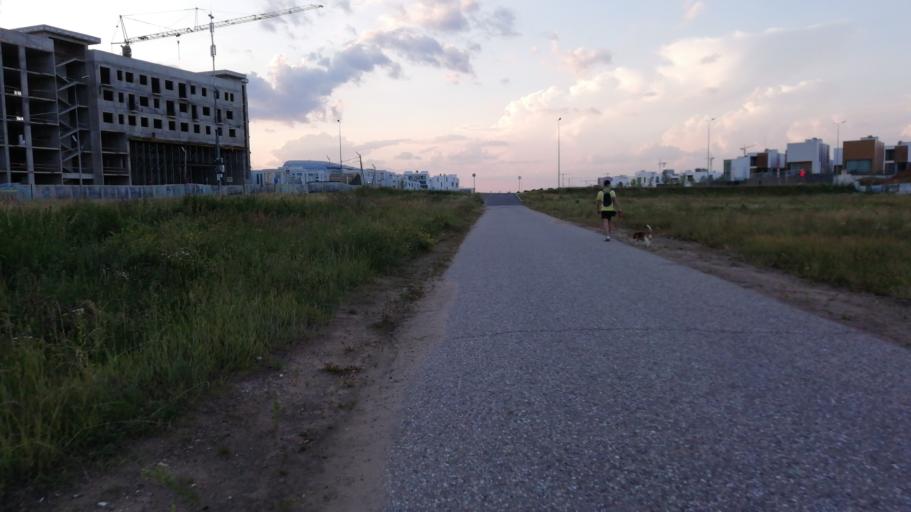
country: RU
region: Moskovskaya
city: Skolkovo
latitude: 55.6885
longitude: 37.3530
